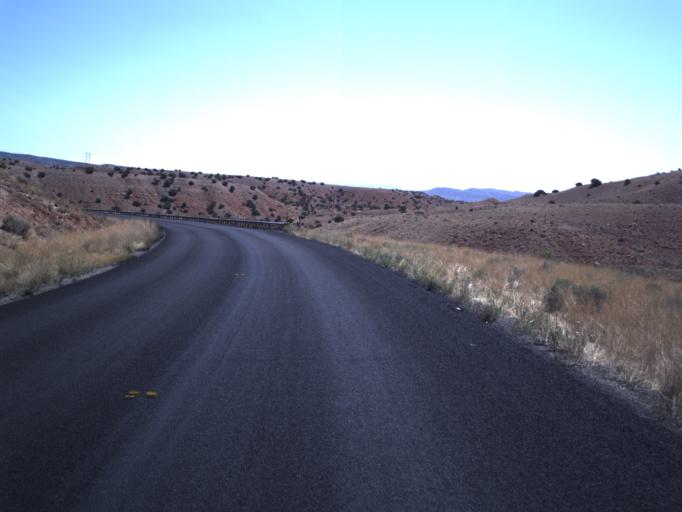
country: US
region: Utah
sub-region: Uintah County
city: Maeser
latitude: 40.4090
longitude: -109.7024
